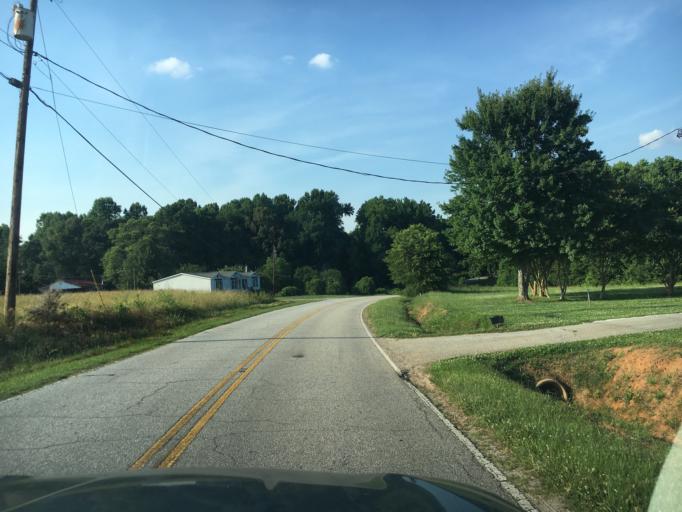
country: US
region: South Carolina
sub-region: Spartanburg County
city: Duncan
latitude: 34.8568
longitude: -82.1188
